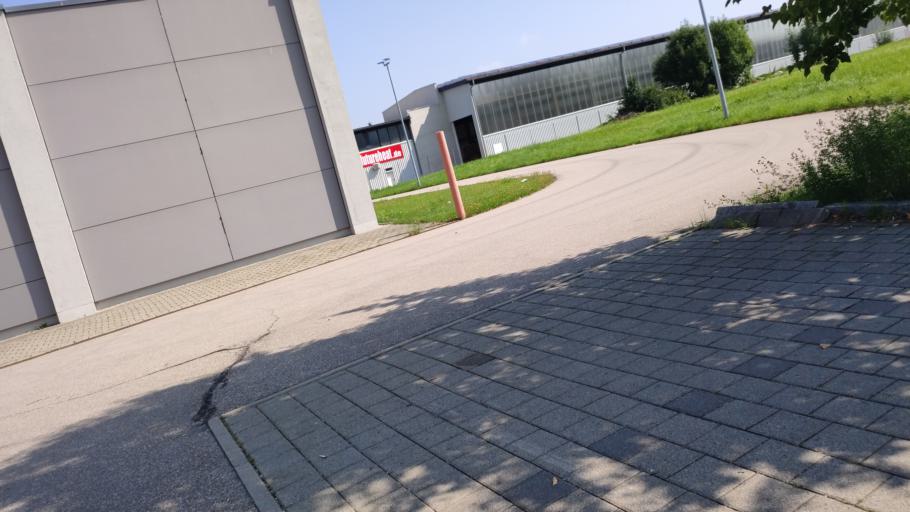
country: DE
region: Bavaria
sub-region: Swabia
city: Bobingen
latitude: 48.2652
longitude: 10.8391
